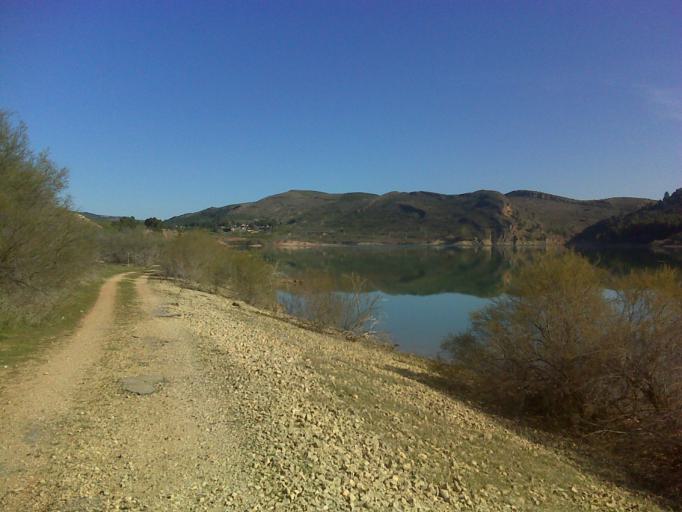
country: ES
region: Aragon
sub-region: Provincia de Zaragoza
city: Nuevalos
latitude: 41.2208
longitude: -1.7918
